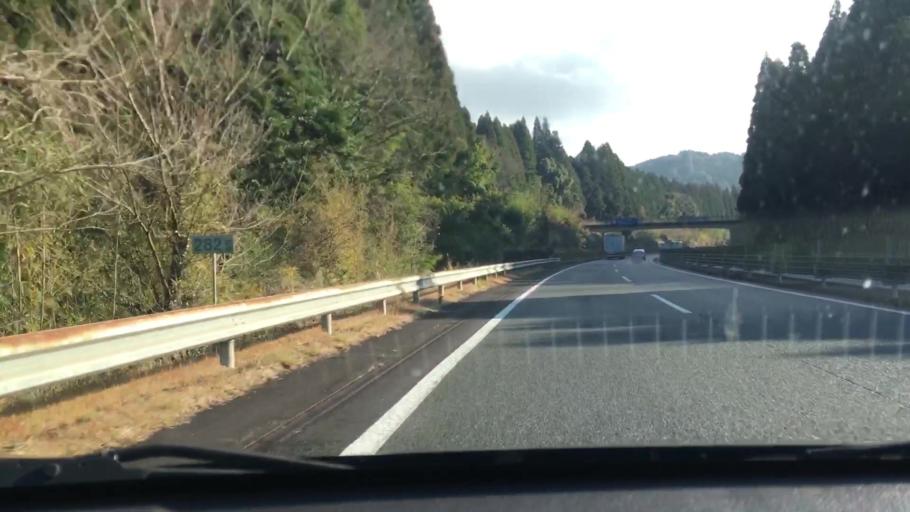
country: JP
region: Kagoshima
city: Okuchi-shinohara
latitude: 31.9995
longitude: 130.7585
